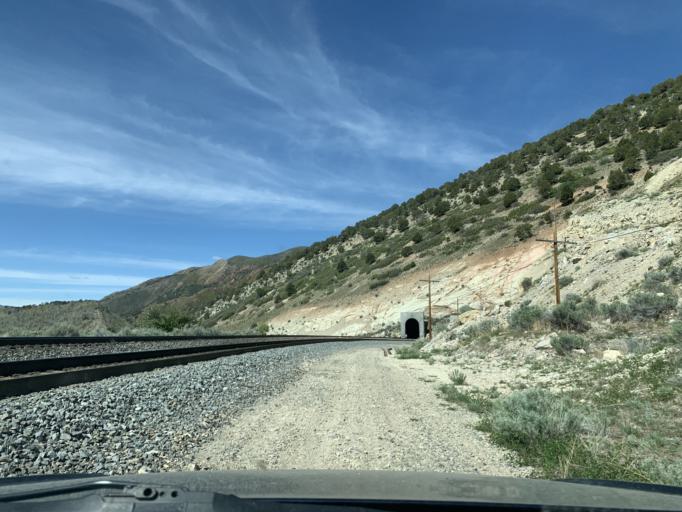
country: US
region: Utah
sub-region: Utah County
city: Mapleton
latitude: 39.9979
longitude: -111.4887
